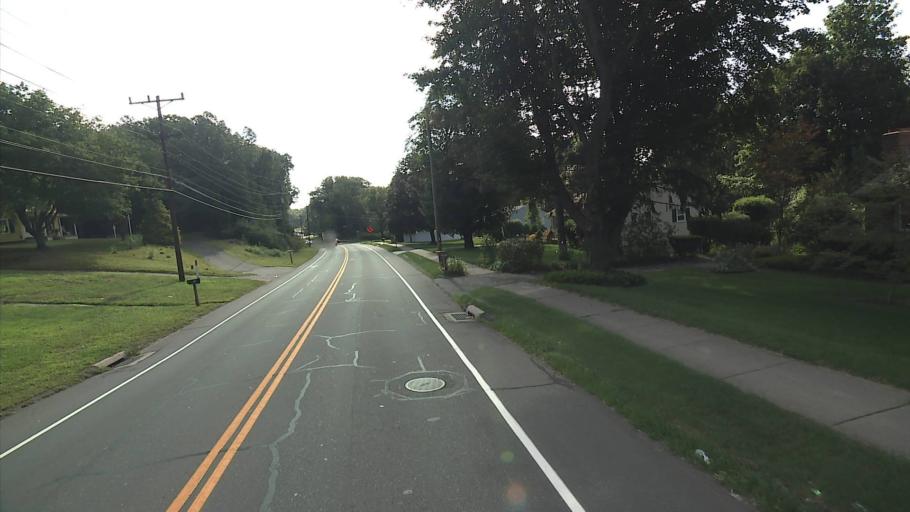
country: US
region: Connecticut
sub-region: Hartford County
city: Hazardville
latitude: 41.9848
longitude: -72.5230
